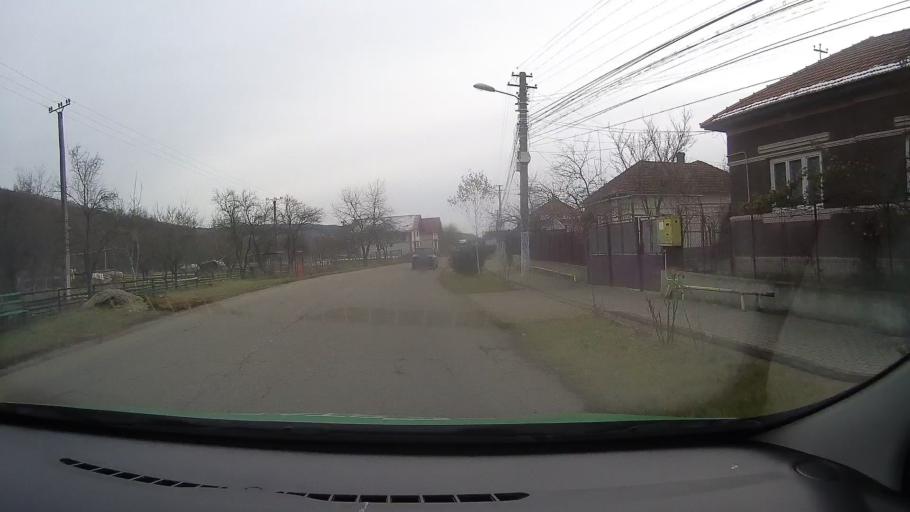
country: RO
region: Hunedoara
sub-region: Comuna Geoagiu
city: Geoagiu
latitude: 45.9339
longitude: 23.1932
